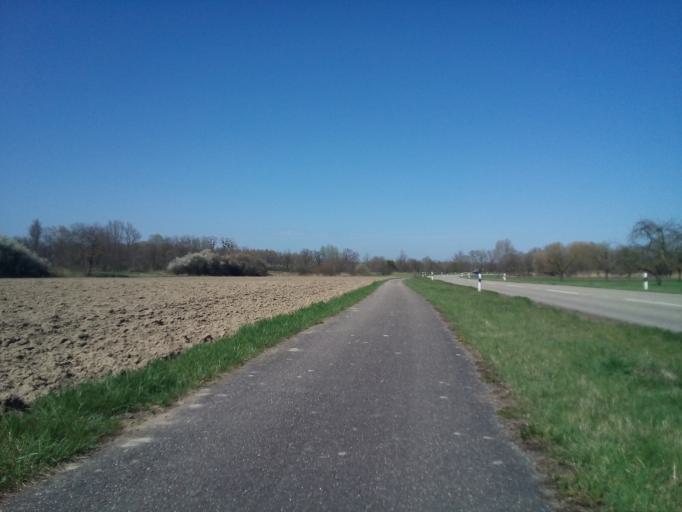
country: FR
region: Alsace
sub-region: Departement du Bas-Rhin
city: La Wantzenau
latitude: 48.6347
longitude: 7.8615
